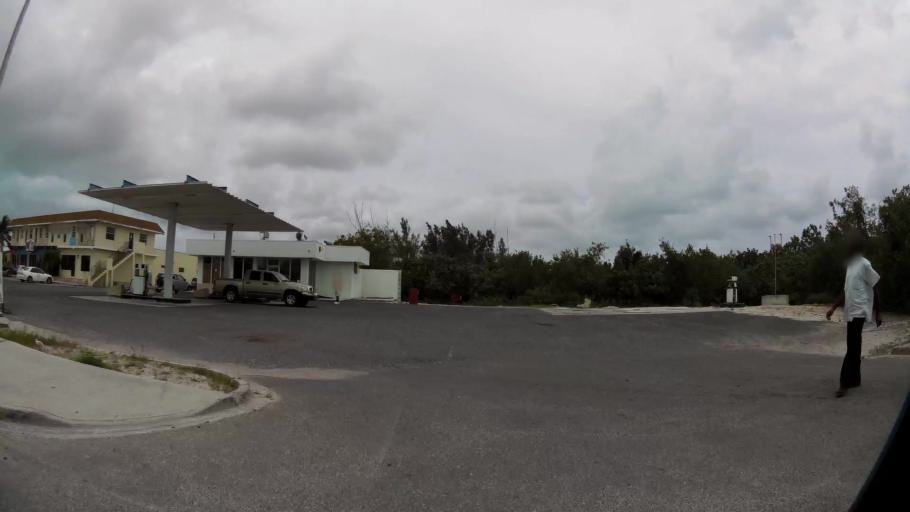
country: BS
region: Mayaguana
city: Abraham's Bay
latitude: 21.7800
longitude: -72.2561
